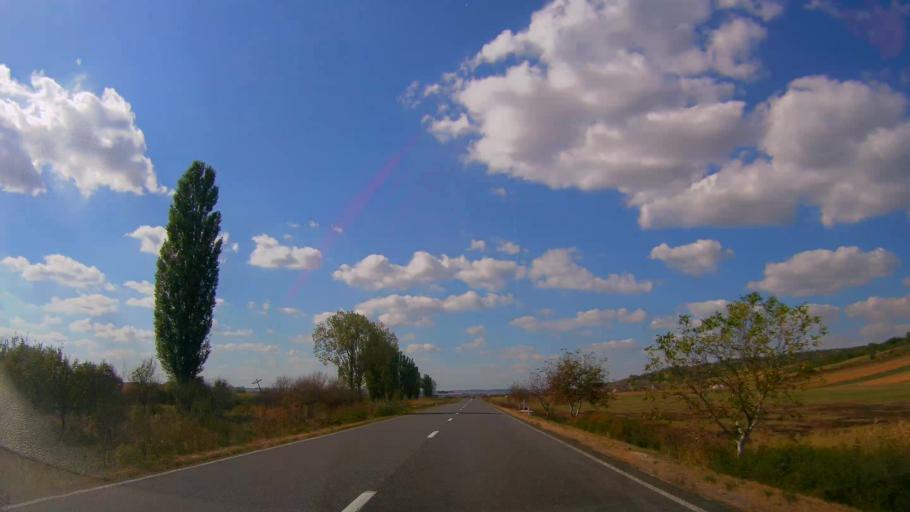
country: RO
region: Salaj
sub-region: Comuna Sarmasag
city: Sarmasag
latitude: 47.3325
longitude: 22.8538
